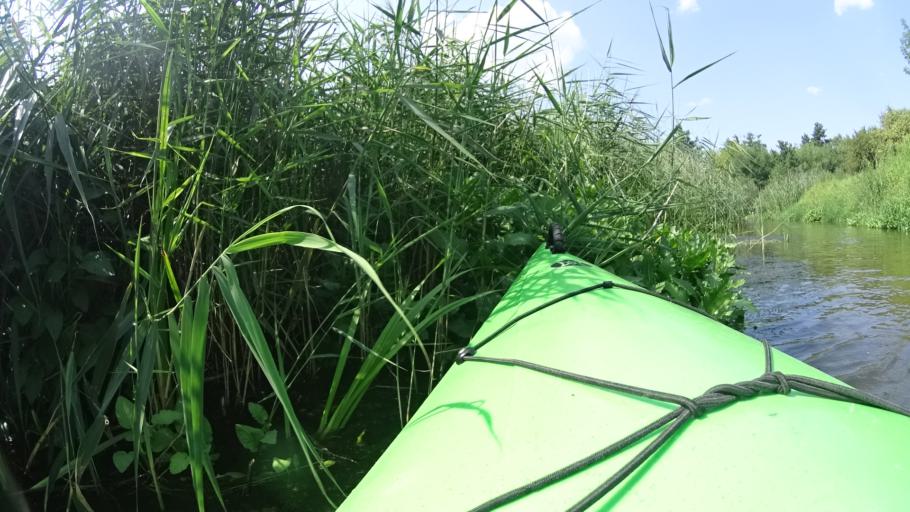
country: PL
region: Masovian Voivodeship
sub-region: Powiat bialobrzeski
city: Wysmierzyce
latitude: 51.6529
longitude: 20.8225
